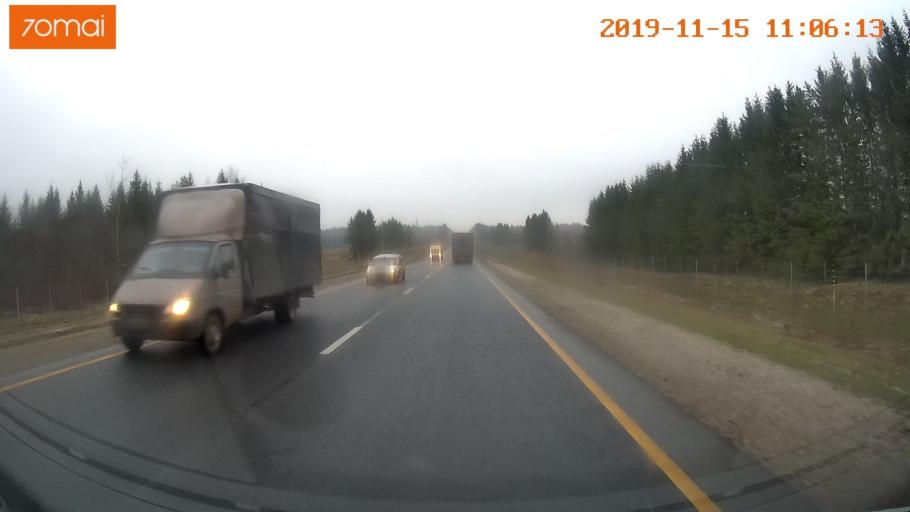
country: RU
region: Vologda
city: Chebsara
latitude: 59.1189
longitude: 39.0222
